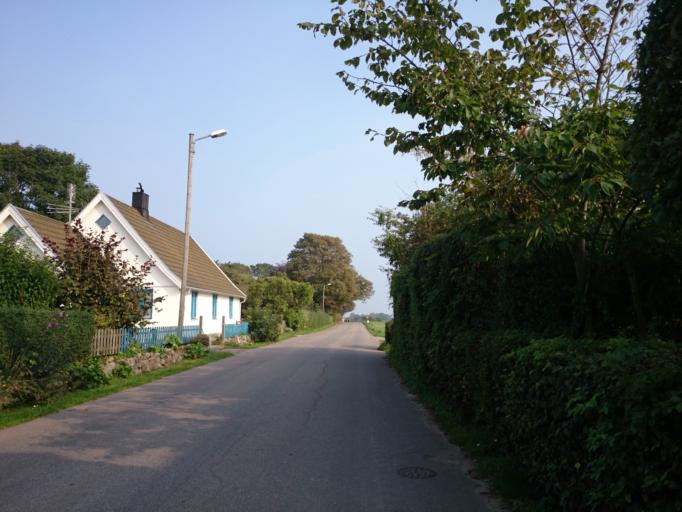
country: SE
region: Skane
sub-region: Helsingborg
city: Rydeback
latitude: 55.9064
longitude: 12.7003
